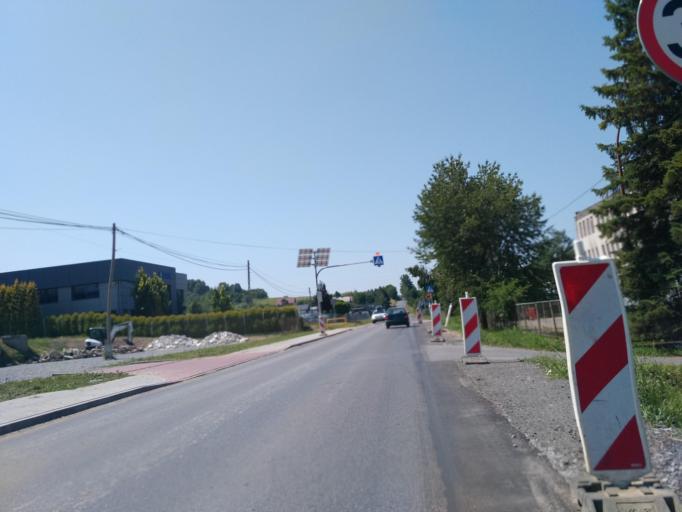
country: PL
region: Subcarpathian Voivodeship
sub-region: Powiat sanocki
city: Sanok
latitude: 49.5617
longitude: 22.1531
